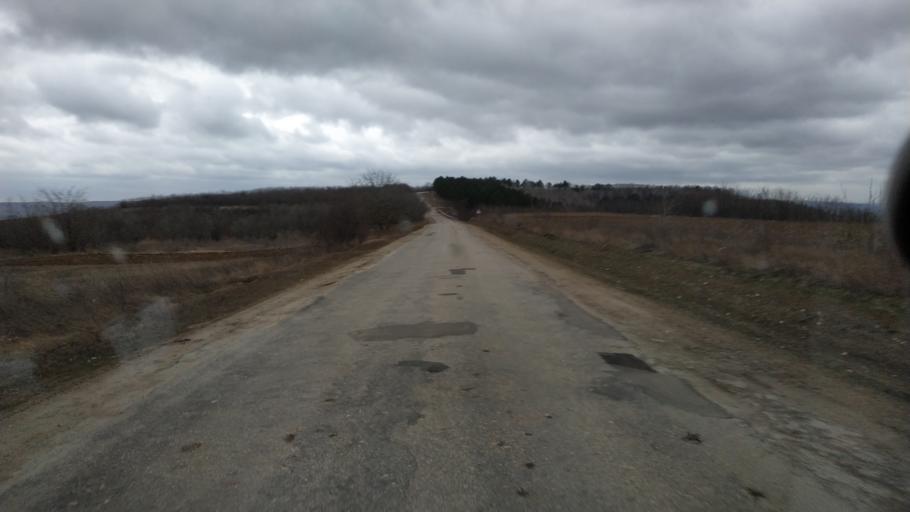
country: MD
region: Calarasi
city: Calarasi
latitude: 47.2213
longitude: 28.2670
